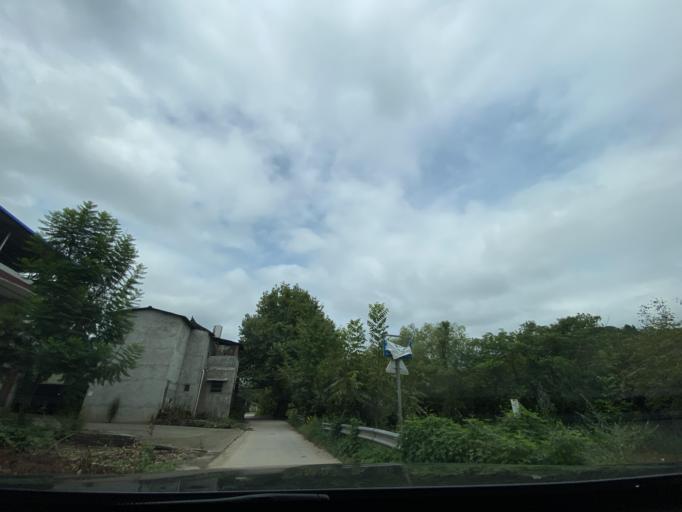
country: CN
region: Sichuan
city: Jiancheng
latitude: 30.3995
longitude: 104.5672
